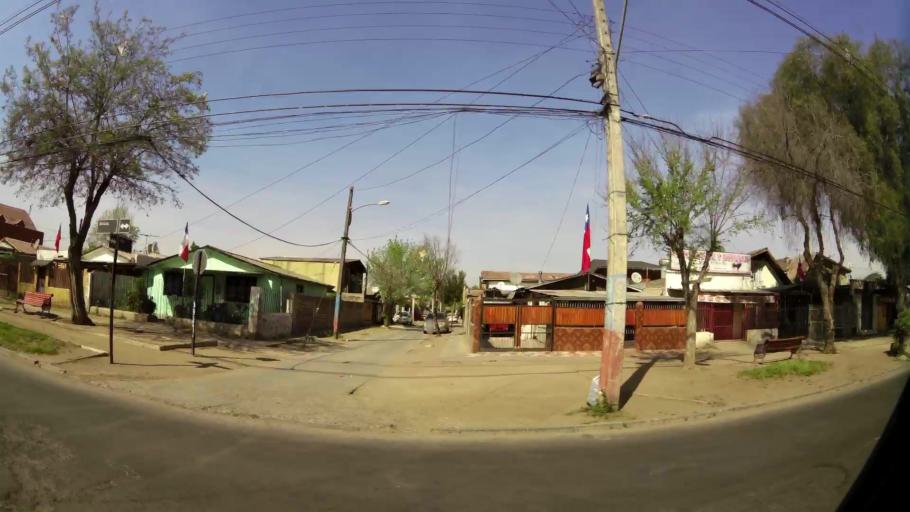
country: CL
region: Santiago Metropolitan
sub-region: Provincia de Santiago
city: Lo Prado
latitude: -33.4313
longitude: -70.7571
